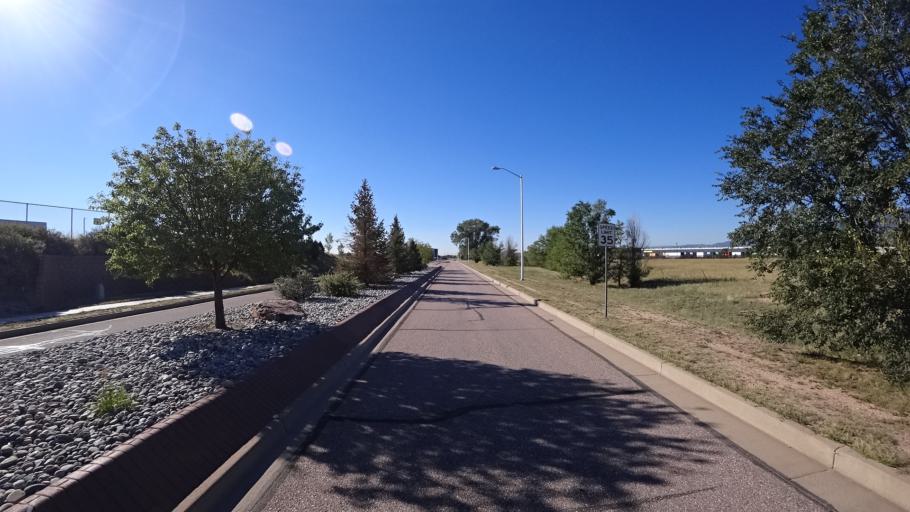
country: US
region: Colorado
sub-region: El Paso County
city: Security-Widefield
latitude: 38.8049
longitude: -104.7237
